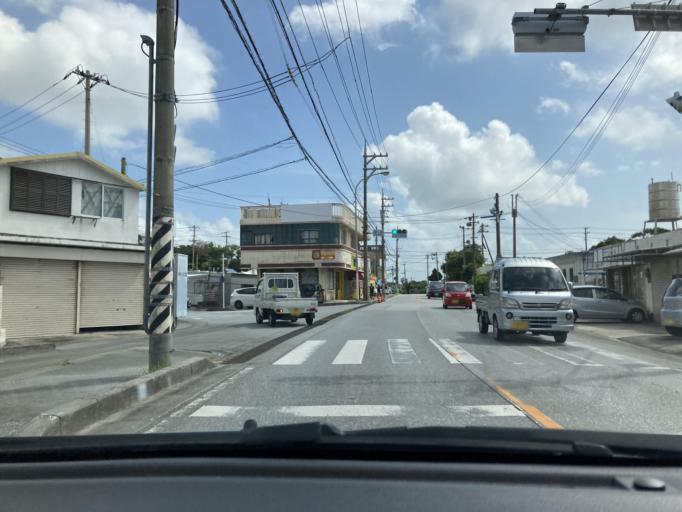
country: JP
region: Okinawa
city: Okinawa
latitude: 26.3181
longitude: 127.8009
